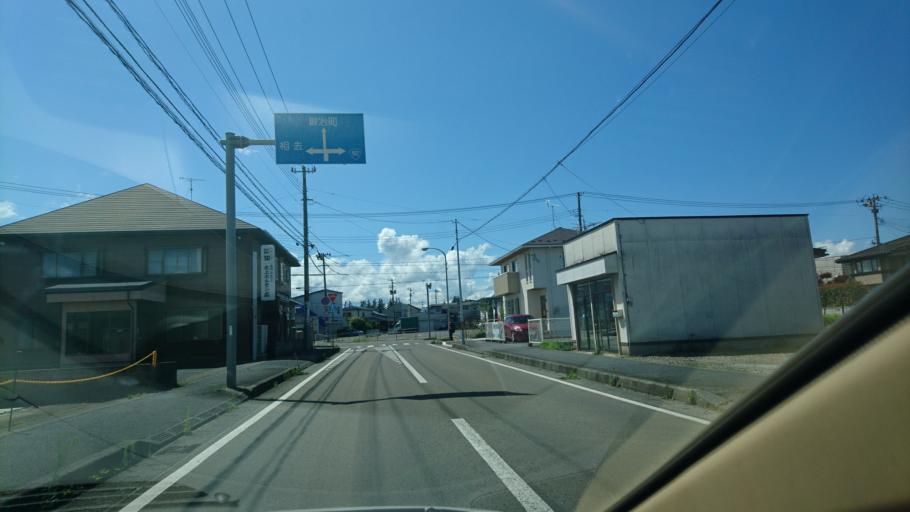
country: JP
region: Iwate
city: Kitakami
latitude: 39.2871
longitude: 141.1097
